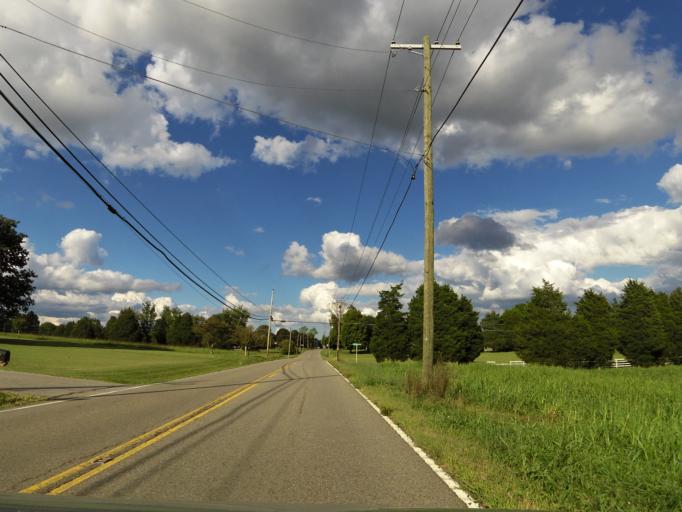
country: US
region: Tennessee
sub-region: Knox County
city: Mascot
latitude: 36.0737
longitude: -83.8346
